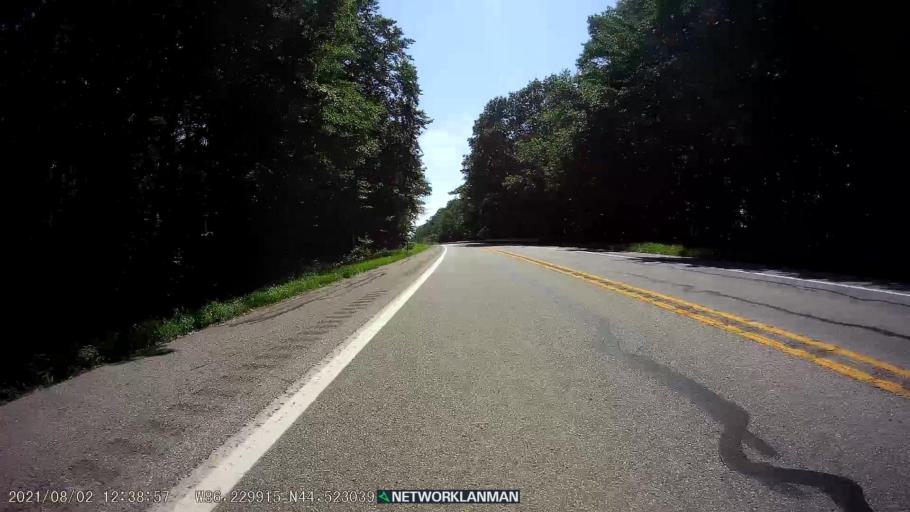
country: US
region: Michigan
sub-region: Benzie County
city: Frankfort
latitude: 44.5231
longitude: -86.2298
